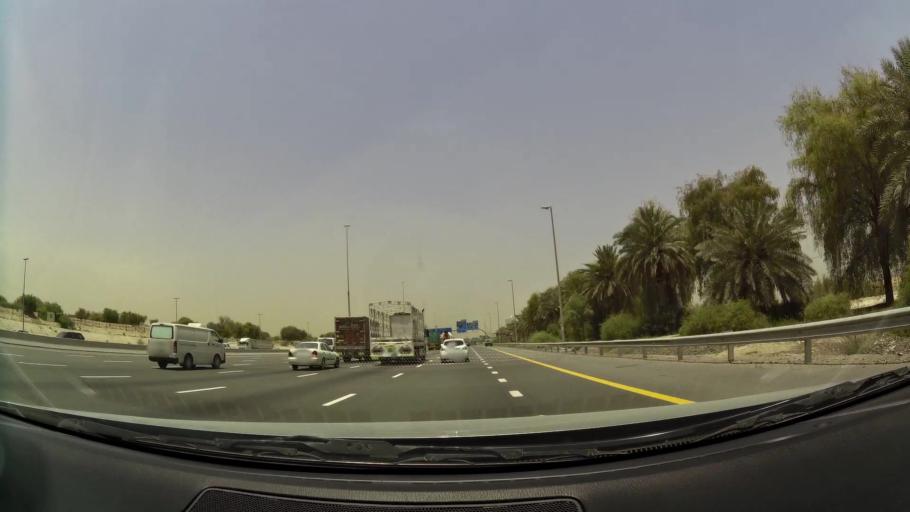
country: AE
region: Dubai
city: Dubai
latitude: 25.0574
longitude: 55.2593
